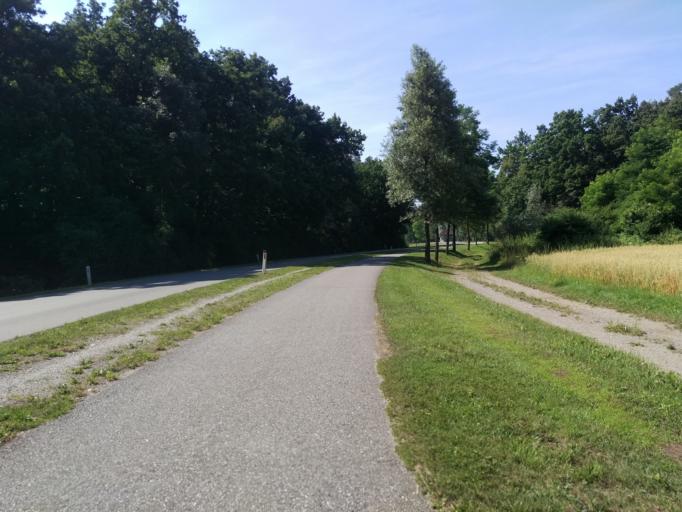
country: AT
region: Styria
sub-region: Politischer Bezirk Graz-Umgebung
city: Feldkirchen bei Graz
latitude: 47.0086
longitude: 15.4682
